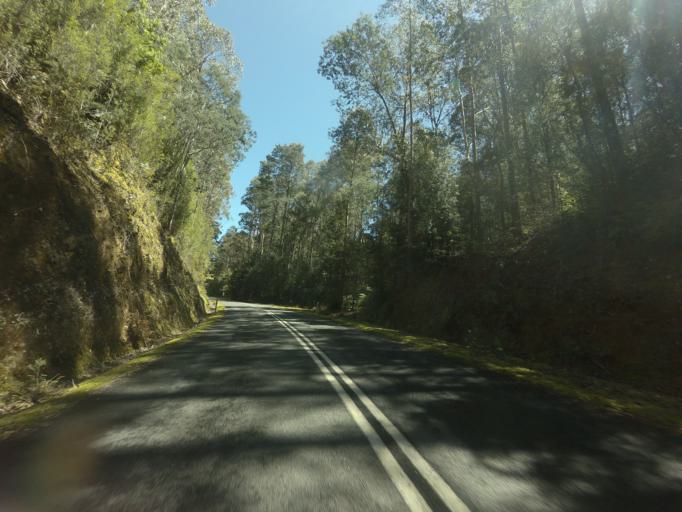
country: AU
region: Tasmania
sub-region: Huon Valley
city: Geeveston
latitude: -42.8190
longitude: 146.3081
